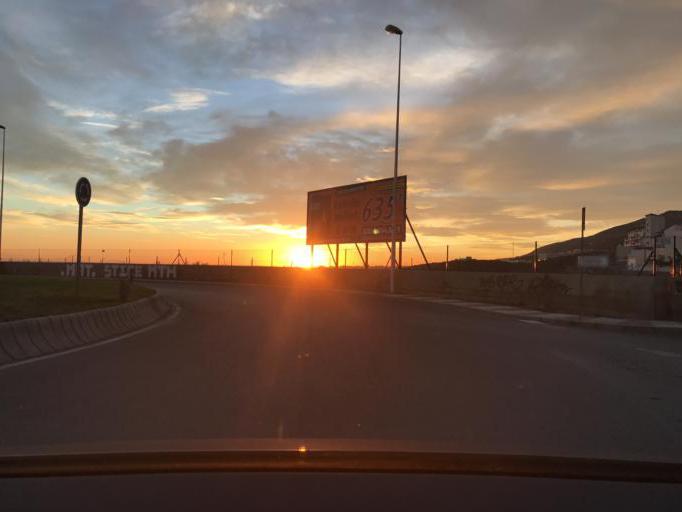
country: ES
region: Andalusia
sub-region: Provincia de Almeria
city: Aguadulce
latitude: 36.8216
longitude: -2.5831
